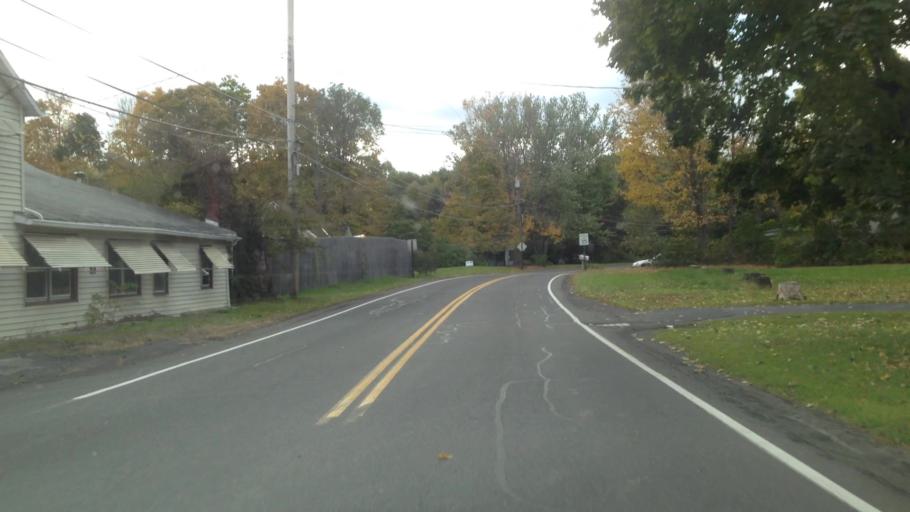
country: US
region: New York
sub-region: Ulster County
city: Tillson
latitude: 41.8281
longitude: -74.0756
